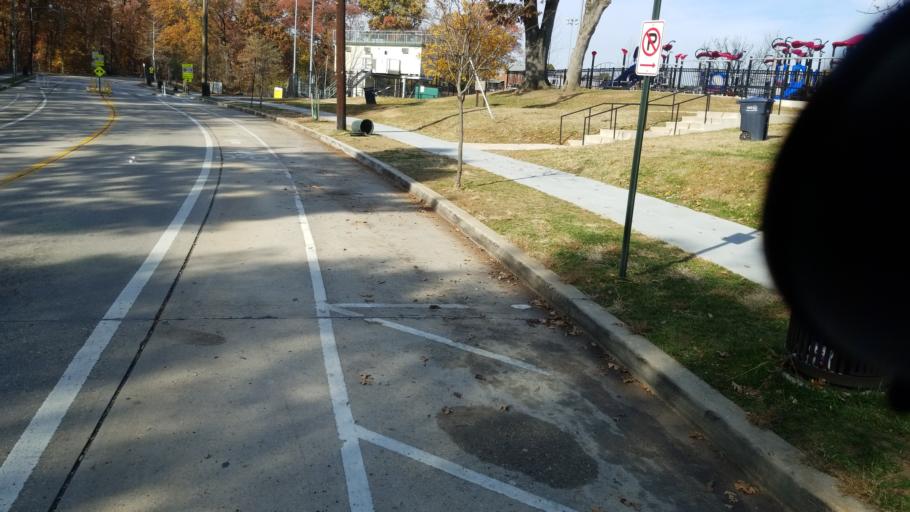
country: US
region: Maryland
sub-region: Prince George's County
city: Coral Hills
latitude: 38.8770
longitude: -76.9422
